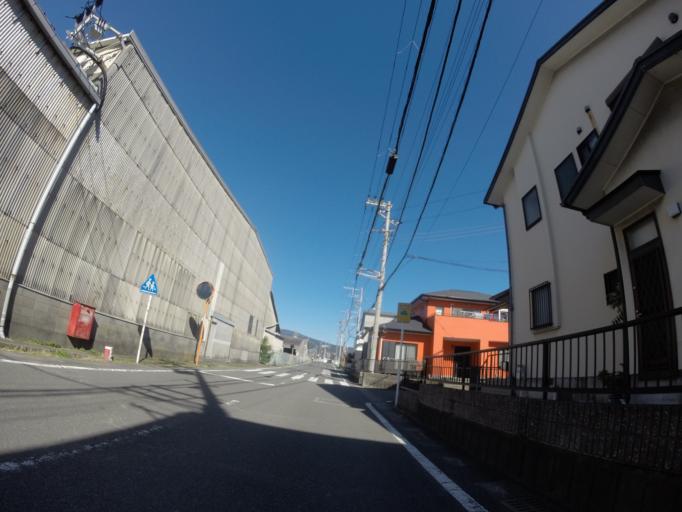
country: JP
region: Shizuoka
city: Numazu
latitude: 35.1239
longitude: 138.8092
